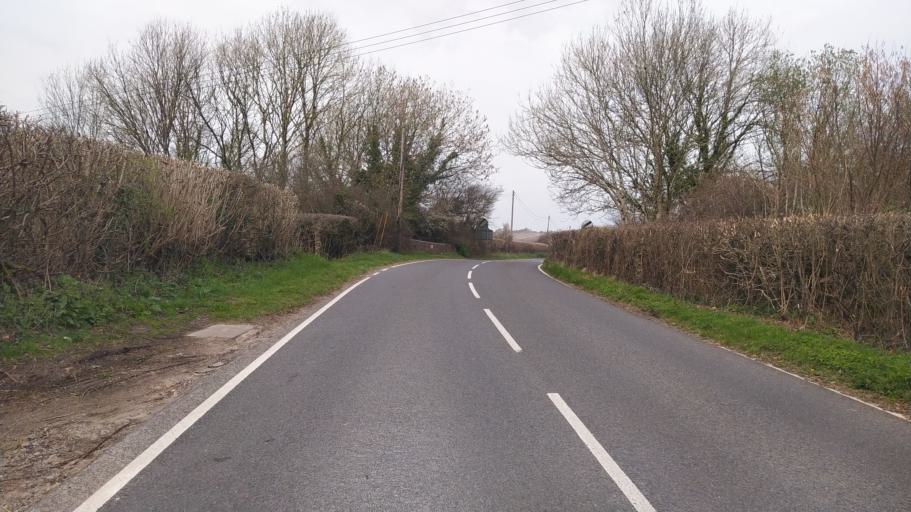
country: GB
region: England
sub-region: Dorset
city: Dorchester
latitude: 50.7777
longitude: -2.5807
